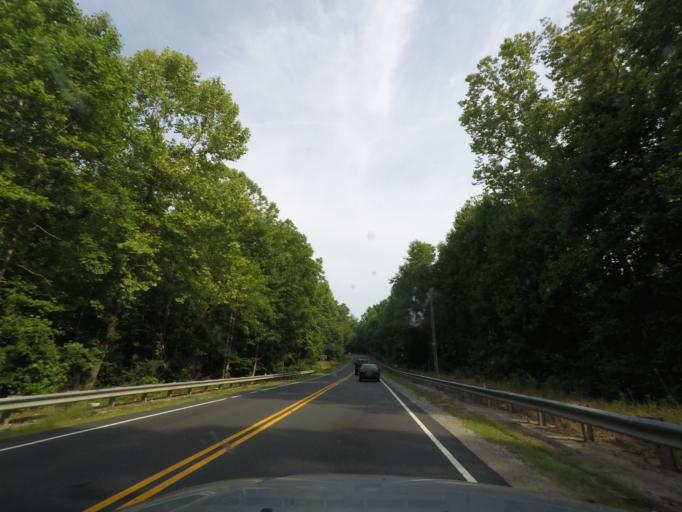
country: US
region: Virginia
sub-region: Prince Edward County
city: Hampden Sydney
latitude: 37.2072
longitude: -78.4431
